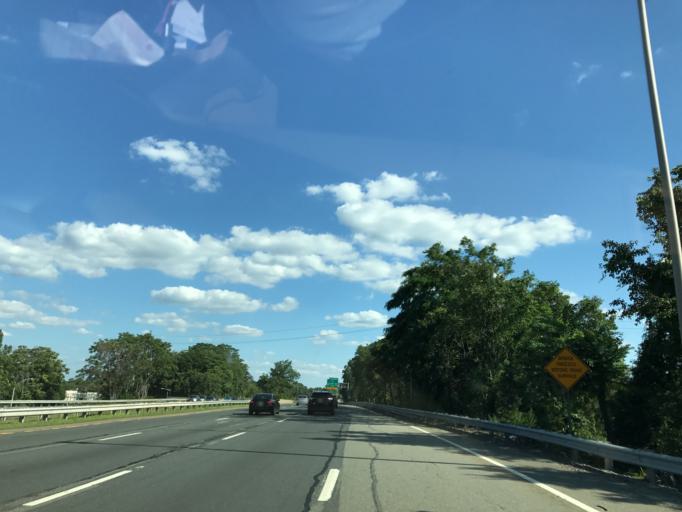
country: US
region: New Jersey
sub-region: Morris County
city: Parsippany
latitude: 40.8720
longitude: -74.4201
